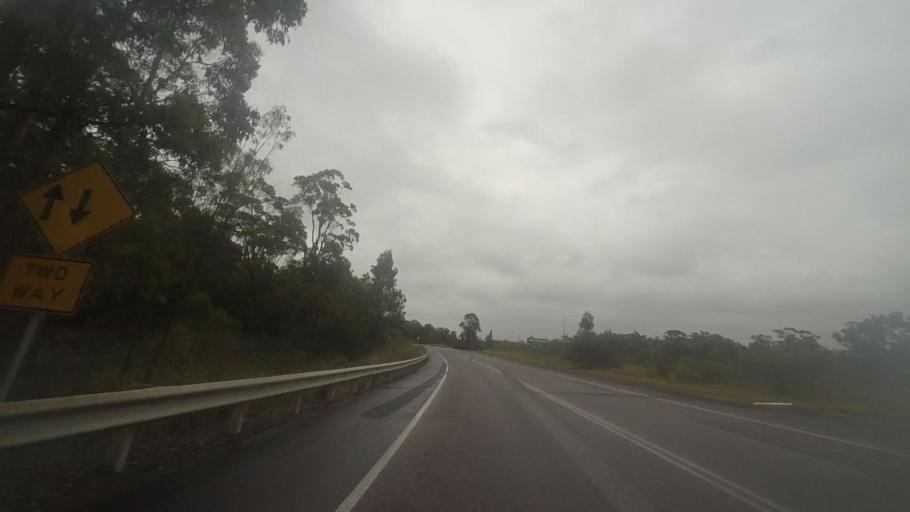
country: AU
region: New South Wales
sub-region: Port Stephens Shire
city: Medowie
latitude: -32.6475
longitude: 151.9184
